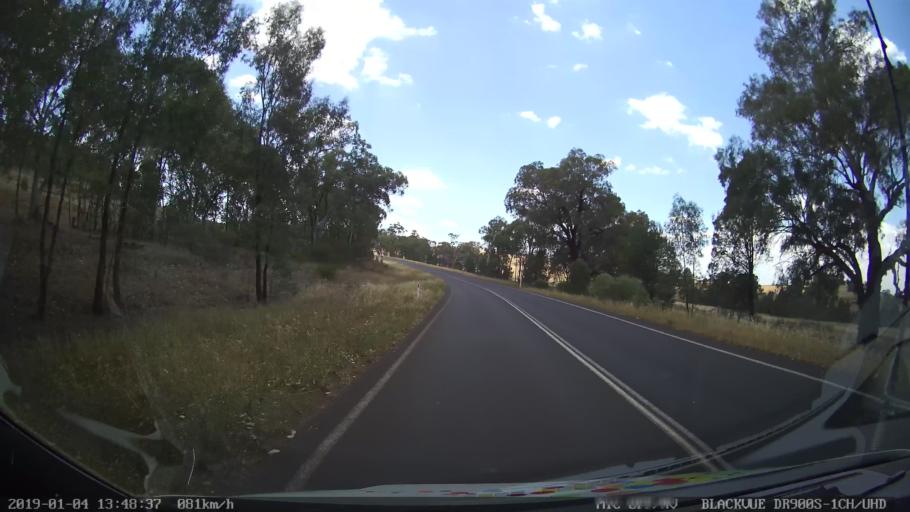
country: AU
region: New South Wales
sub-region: Dubbo Municipality
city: Dubbo
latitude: -32.4404
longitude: 148.5845
